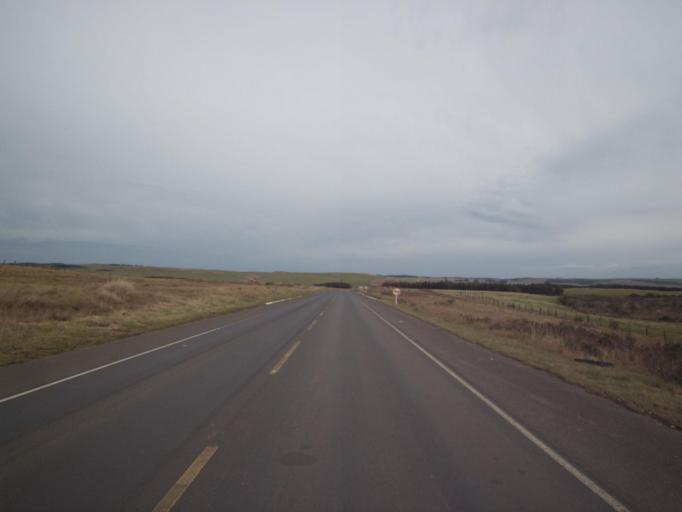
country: BR
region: Parana
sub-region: Palmas
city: Palmas
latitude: -26.7522
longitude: -51.6631
